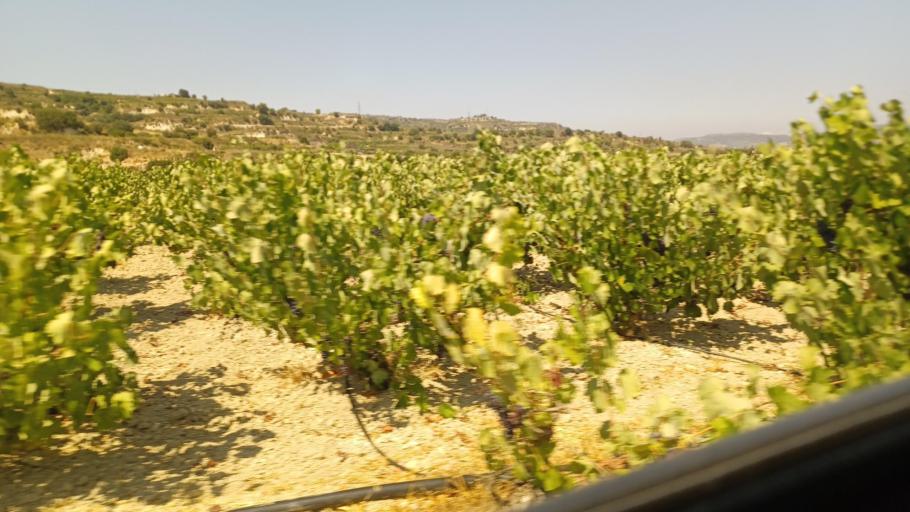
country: CY
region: Pafos
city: Mesogi
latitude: 34.8629
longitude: 32.4990
